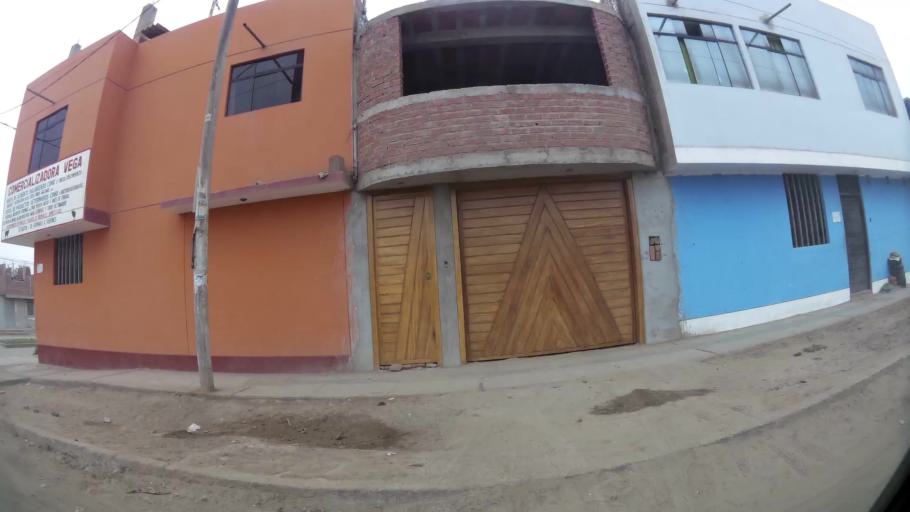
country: PE
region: La Libertad
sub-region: Provincia de Trujillo
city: Buenos Aires
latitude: -8.1485
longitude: -79.0473
